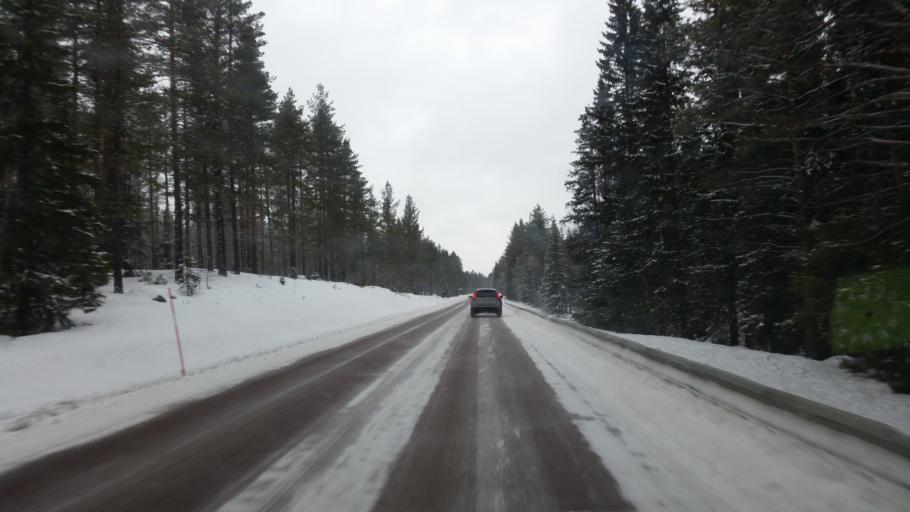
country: SE
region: Jaemtland
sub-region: Bergs Kommun
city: Hoverberg
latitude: 62.4177
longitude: 14.6120
